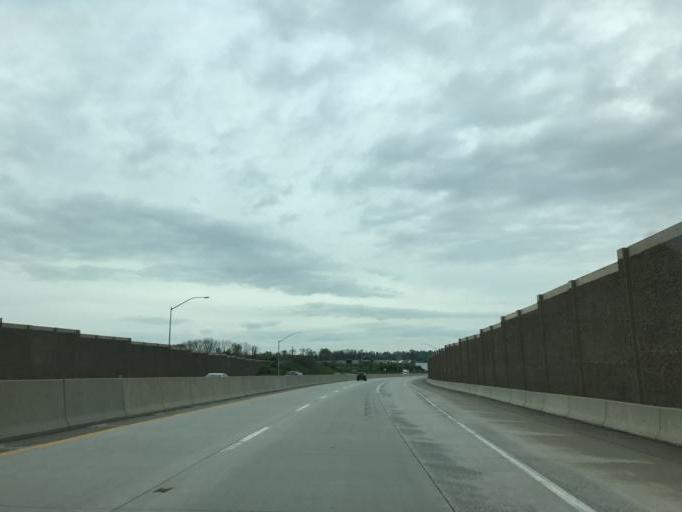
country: US
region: Pennsylvania
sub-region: Berks County
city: Montrose
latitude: 40.3087
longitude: -75.9990
